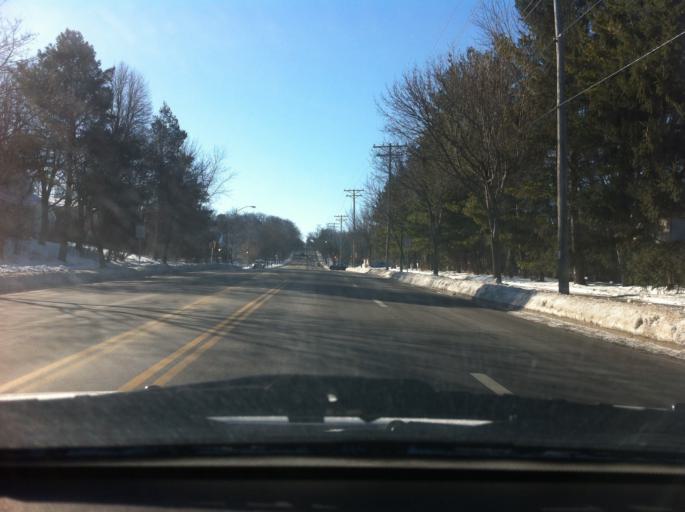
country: US
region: Wisconsin
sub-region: Dane County
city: Middleton
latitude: 43.0779
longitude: -89.5023
